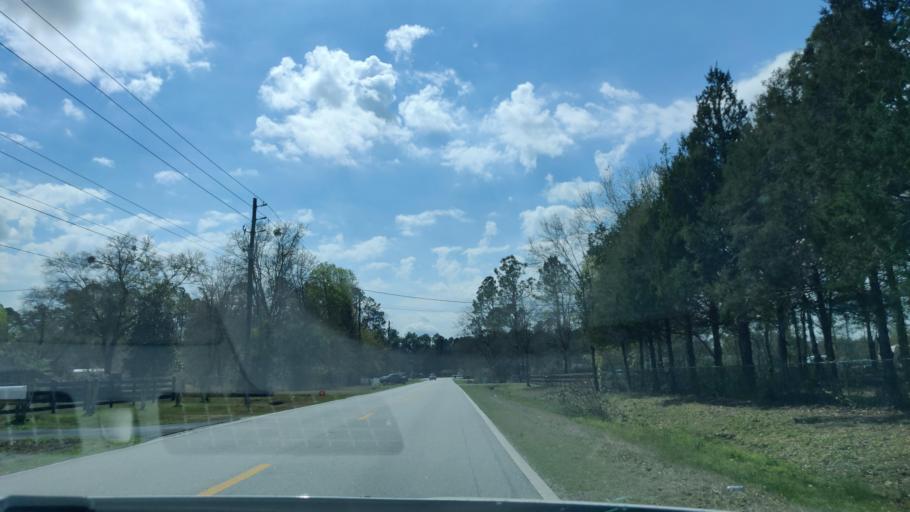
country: US
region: Florida
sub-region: Duval County
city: Baldwin
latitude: 30.2212
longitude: -81.9410
